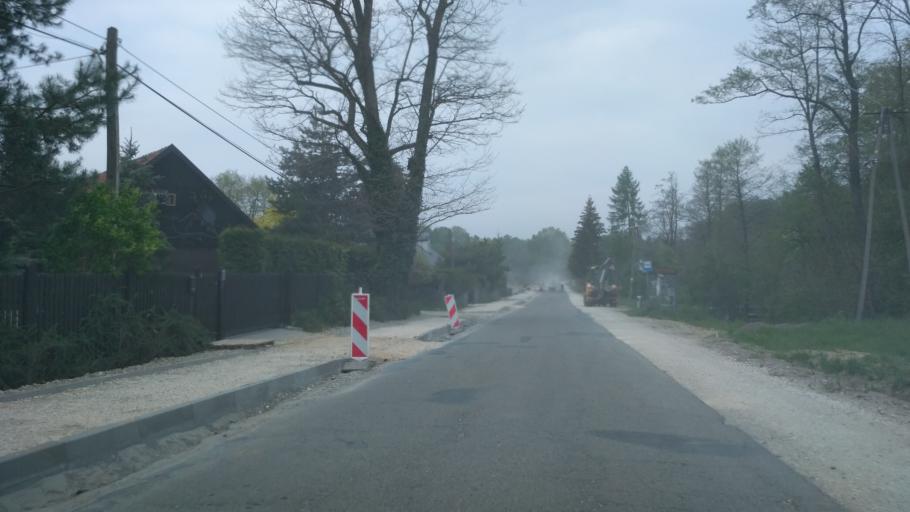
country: PL
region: Lesser Poland Voivodeship
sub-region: Powiat tarnowski
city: Skrzyszow
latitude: 49.9819
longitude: 21.0642
